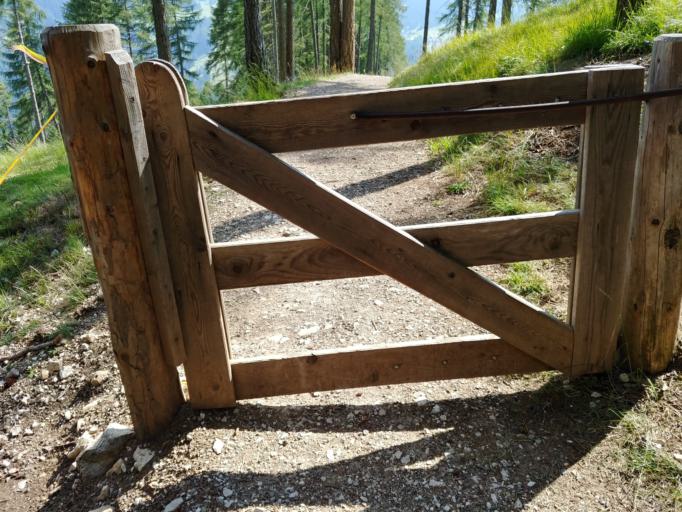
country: IT
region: Trentino-Alto Adige
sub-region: Bolzano
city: Santa Cristina Valgardena
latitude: 46.5698
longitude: 11.7296
